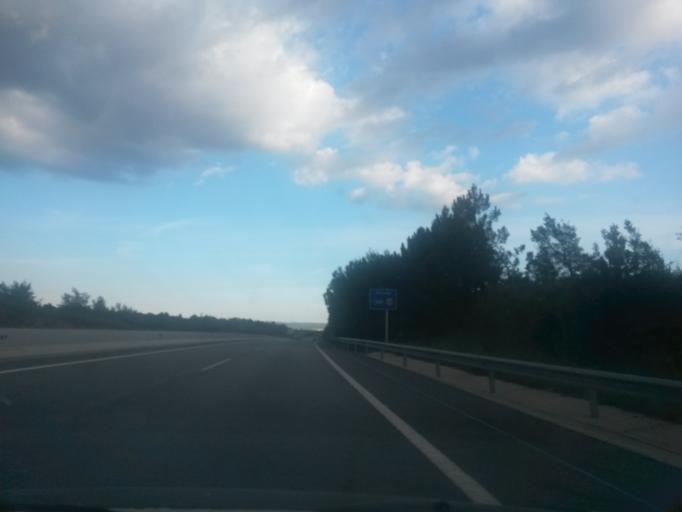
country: ES
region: Catalonia
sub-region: Provincia de Girona
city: Brunyola
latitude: 41.8794
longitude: 2.7035
